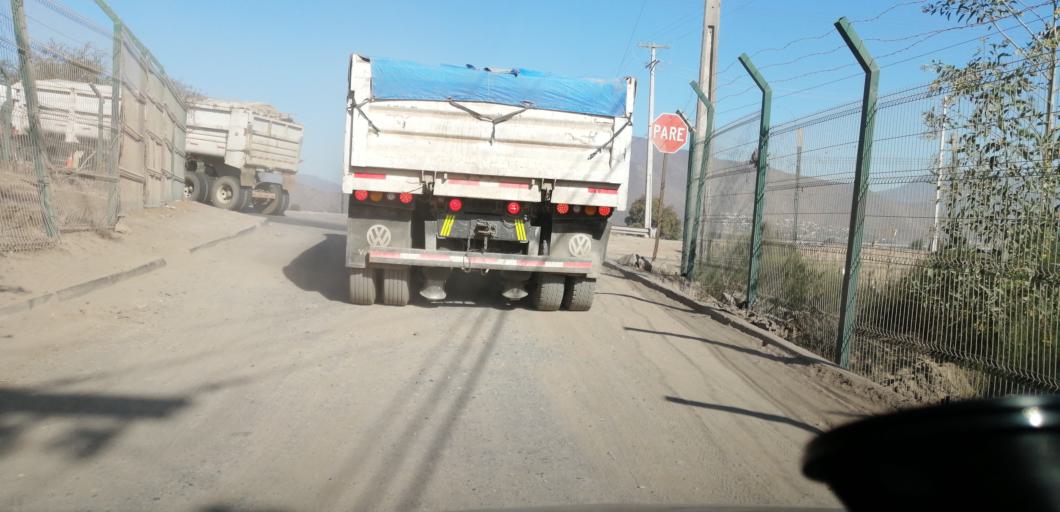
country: CL
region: Santiago Metropolitan
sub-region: Provincia de Santiago
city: Lo Prado
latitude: -33.4628
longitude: -70.7830
